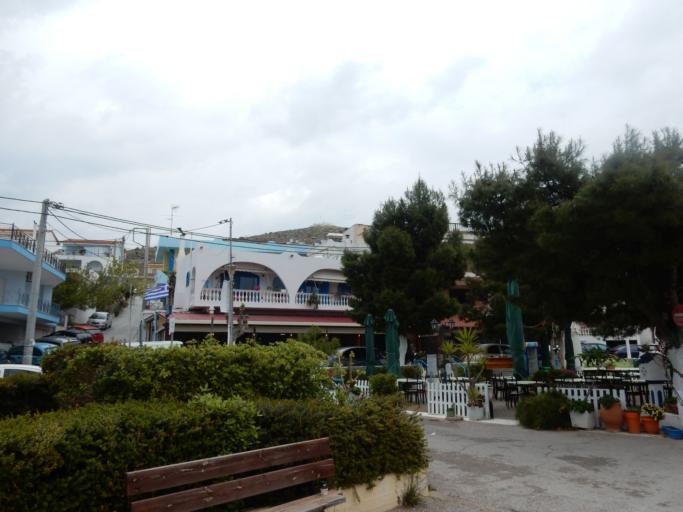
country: GR
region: Attica
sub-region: Nomarchia Dytikis Attikis
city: Megara
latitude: 37.9739
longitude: 23.3624
